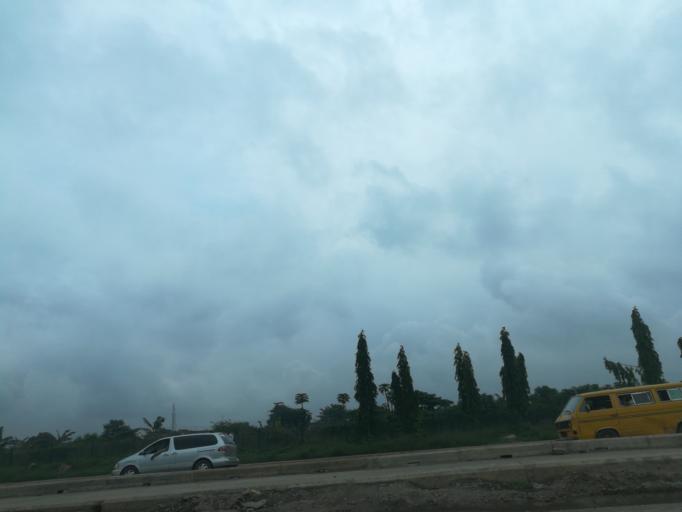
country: NG
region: Lagos
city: Oshodi
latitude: 6.5663
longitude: 3.3474
